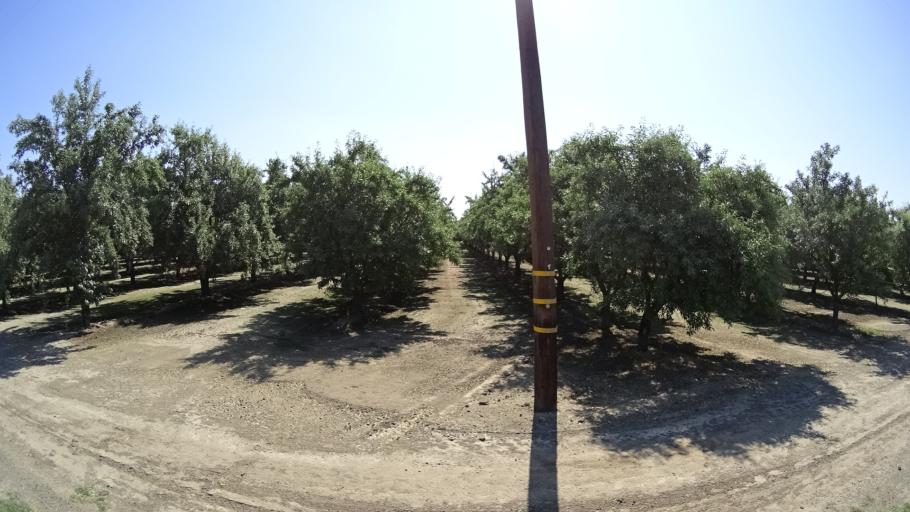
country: US
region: California
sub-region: Kings County
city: Lucerne
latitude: 36.3832
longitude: -119.5830
